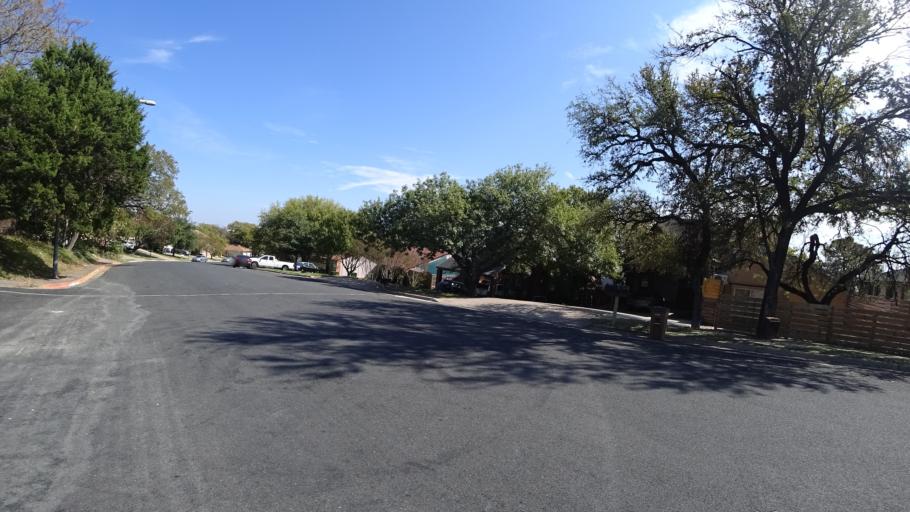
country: US
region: Texas
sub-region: Travis County
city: Shady Hollow
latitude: 30.2101
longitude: -97.8165
